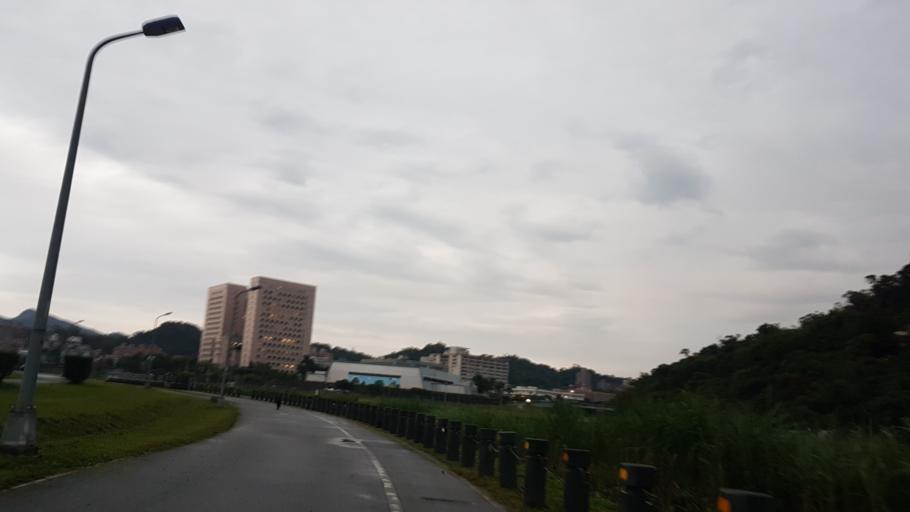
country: TW
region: Taipei
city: Taipei
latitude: 24.9823
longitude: 121.5709
